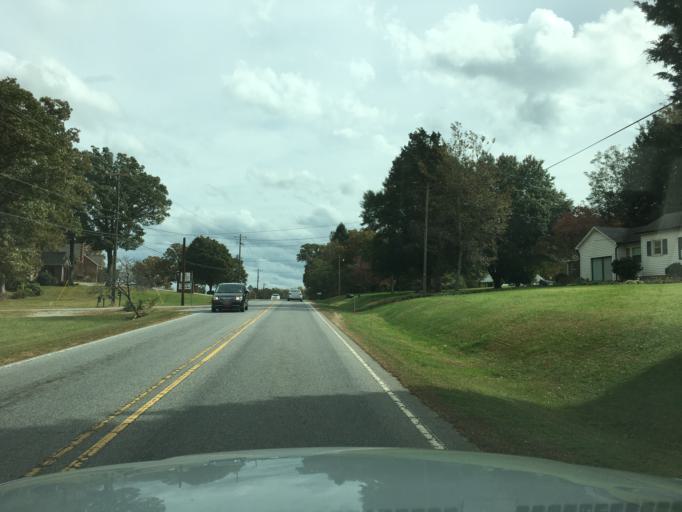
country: US
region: North Carolina
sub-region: Catawba County
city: Hickory
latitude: 35.6933
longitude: -81.2861
